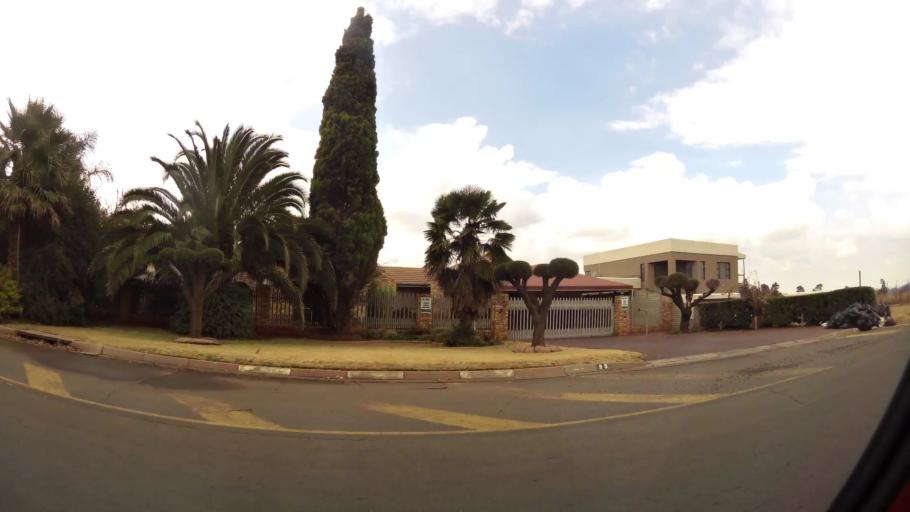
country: ZA
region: Gauteng
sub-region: Sedibeng District Municipality
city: Vanderbijlpark
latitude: -26.7364
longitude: 27.8549
